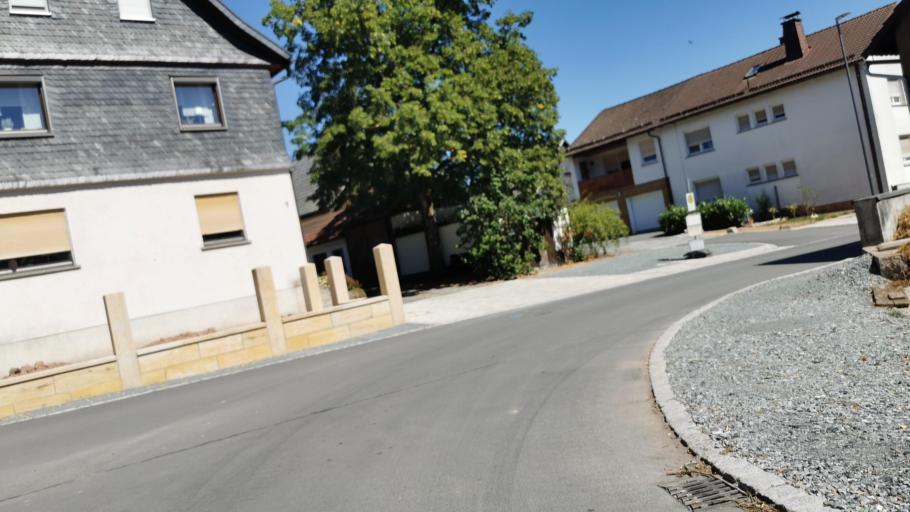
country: DE
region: Bavaria
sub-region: Upper Franconia
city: Pressig
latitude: 50.3711
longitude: 11.3011
